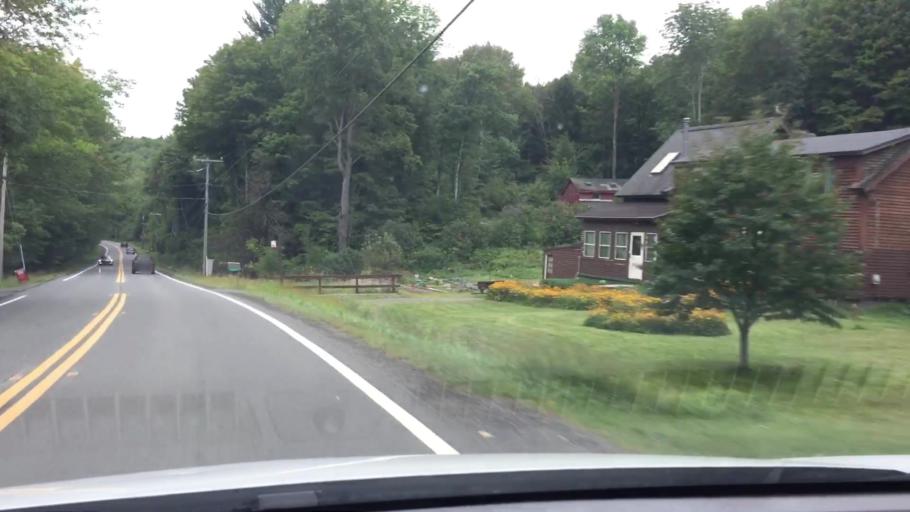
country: US
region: Massachusetts
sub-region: Berkshire County
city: Hinsdale
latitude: 42.3839
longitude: -73.1225
